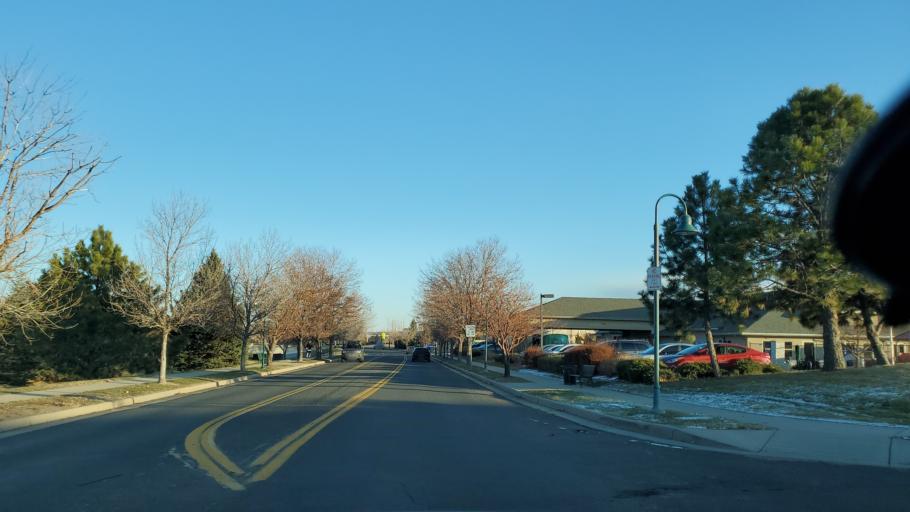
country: US
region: Colorado
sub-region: Broomfield County
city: Broomfield
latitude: 39.9157
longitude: -105.0624
